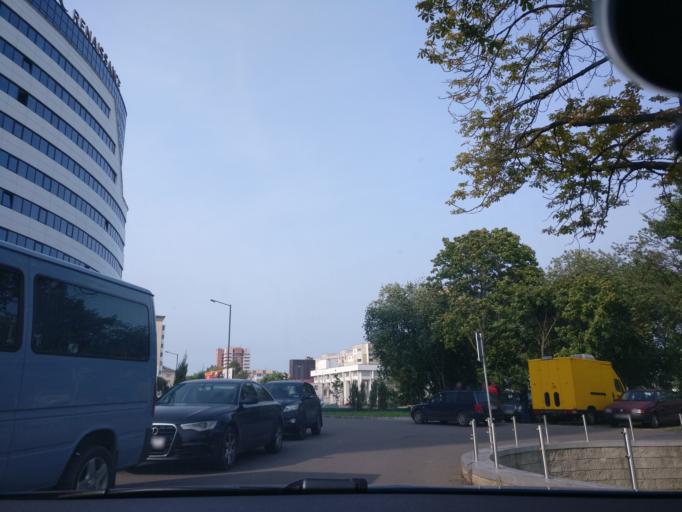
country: BY
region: Minsk
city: Minsk
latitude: 53.8921
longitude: 27.5300
